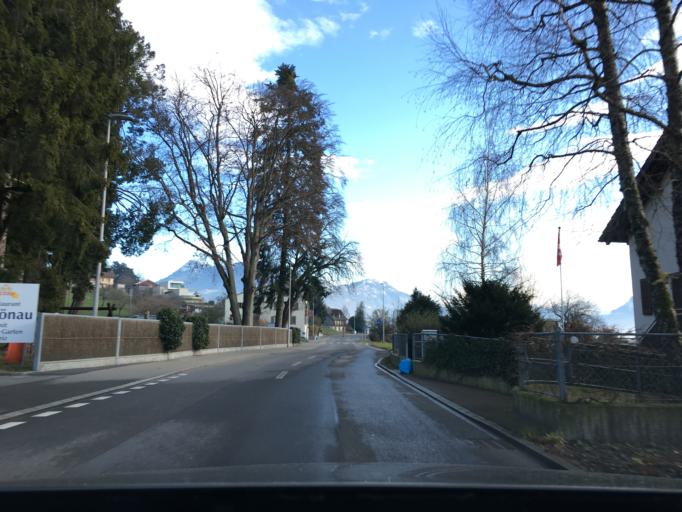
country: CH
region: Lucerne
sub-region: Lucerne-Land District
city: Adligenswil
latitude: 47.0508
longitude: 8.3593
